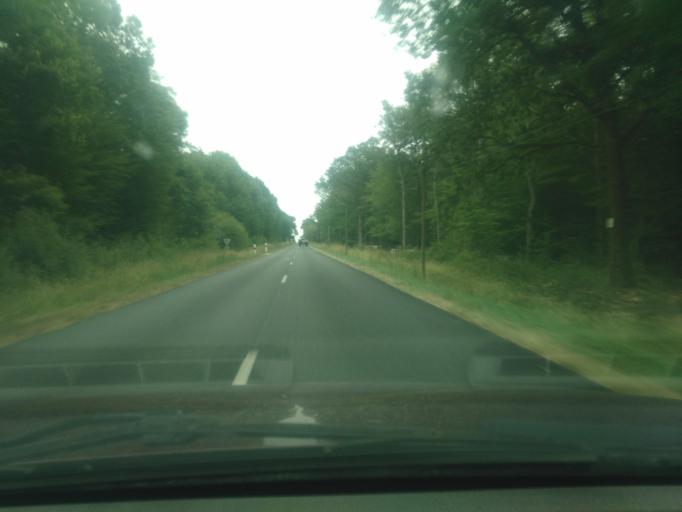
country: FR
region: Bourgogne
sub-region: Departement de la Nievre
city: Dornes
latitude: 46.7741
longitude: 3.2934
